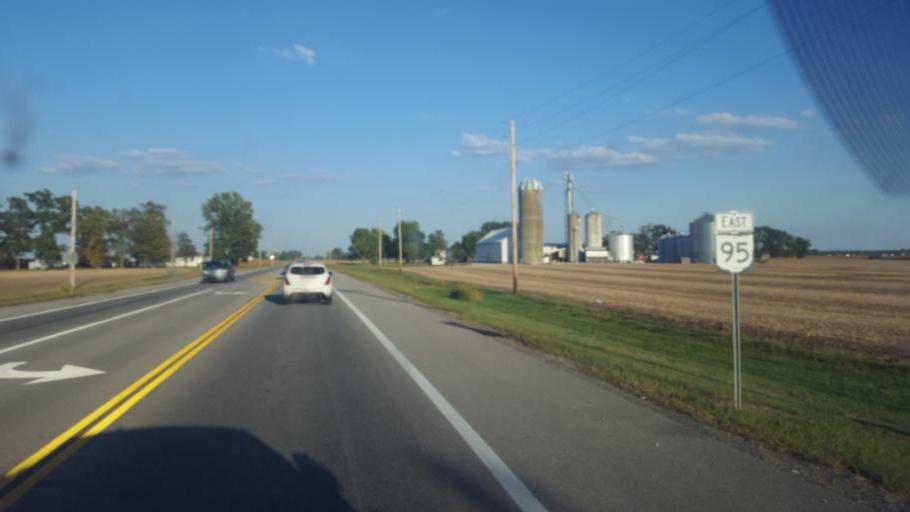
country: US
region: Ohio
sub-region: Marion County
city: Marion
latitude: 40.5821
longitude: -83.0397
